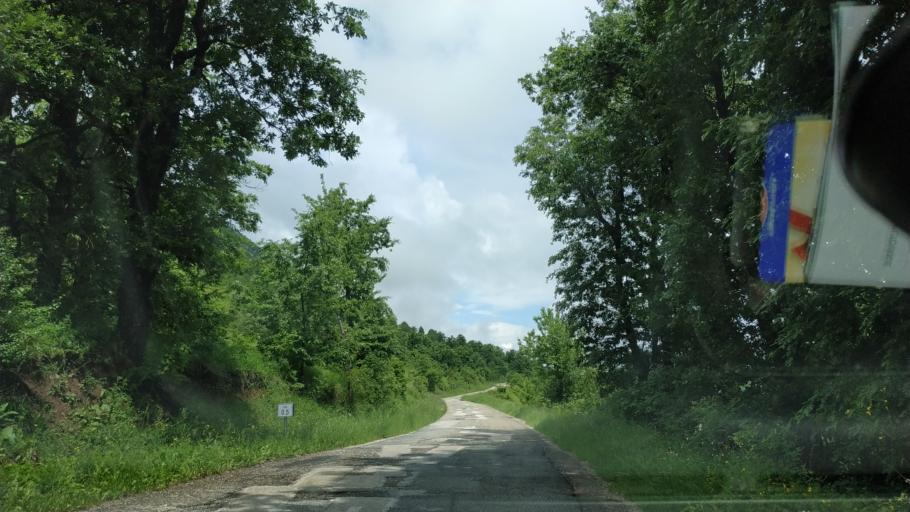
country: RS
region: Central Serbia
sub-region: Zajecarski Okrug
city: Boljevac
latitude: 43.7389
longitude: 21.9507
